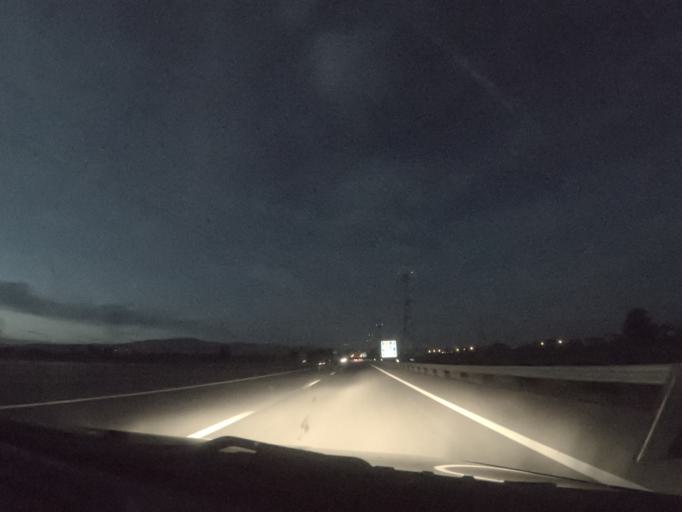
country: PT
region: Guarda
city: Alcains
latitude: 39.9700
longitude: -7.4584
